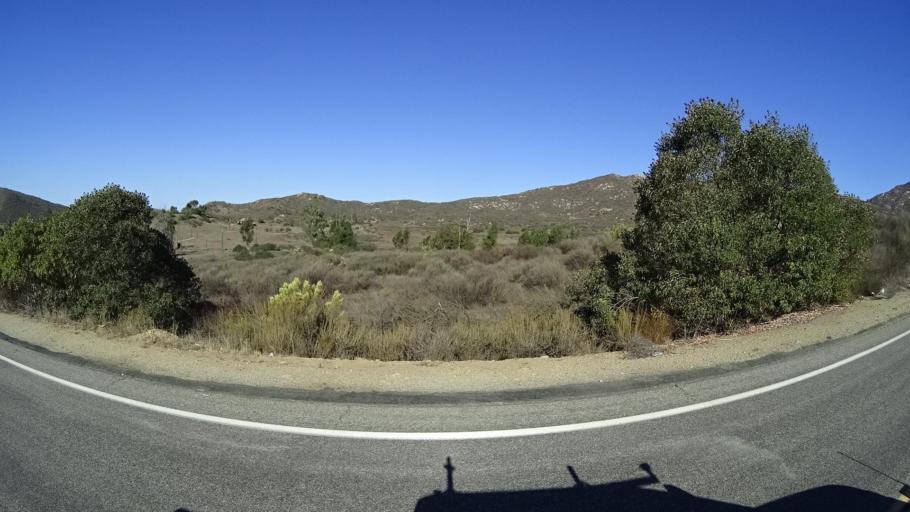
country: US
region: California
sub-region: San Diego County
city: Jamul
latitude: 32.6677
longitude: -116.7849
